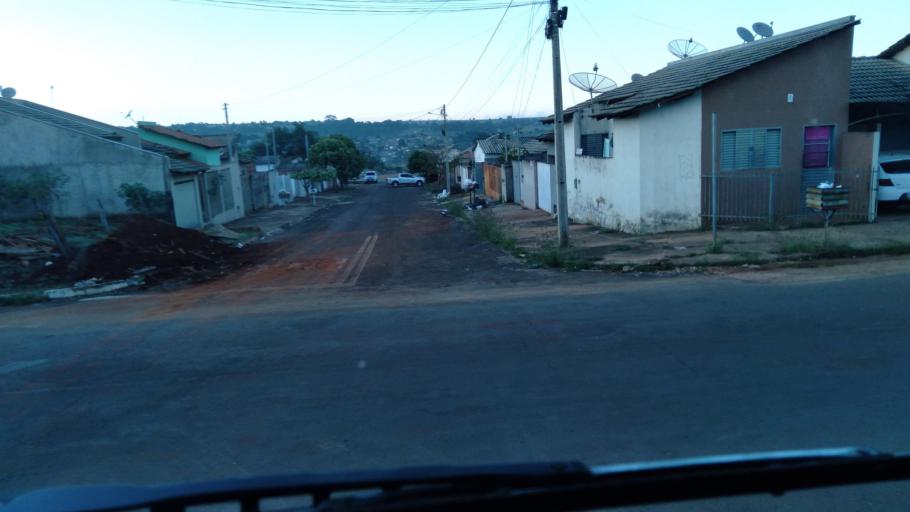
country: BR
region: Goias
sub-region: Mineiros
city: Mineiros
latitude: -17.5750
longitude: -52.5703
